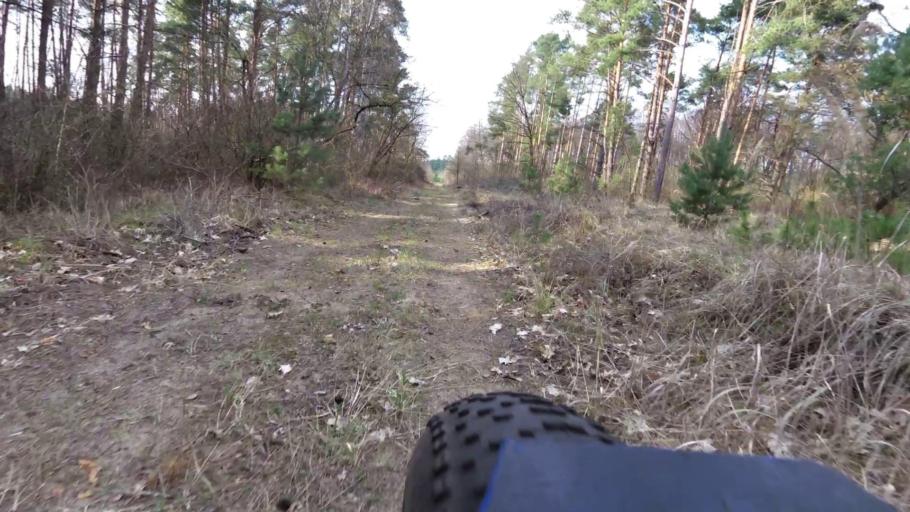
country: PL
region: Lubusz
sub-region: Powiat slubicki
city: Cybinka
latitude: 52.2387
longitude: 14.7744
